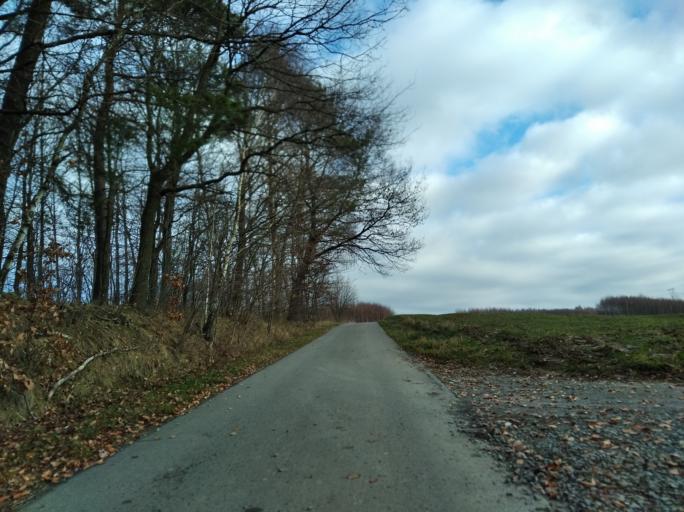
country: PL
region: Subcarpathian Voivodeship
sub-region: Powiat strzyzowski
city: Strzyzow
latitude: 49.8830
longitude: 21.8375
